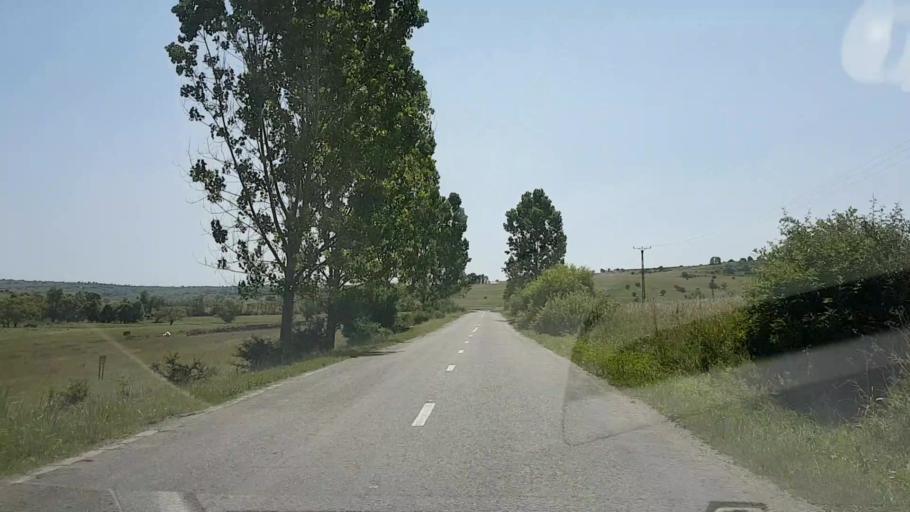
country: RO
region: Sibiu
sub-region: Comuna Merghindeal
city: Merghindeal
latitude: 45.9600
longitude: 24.7563
